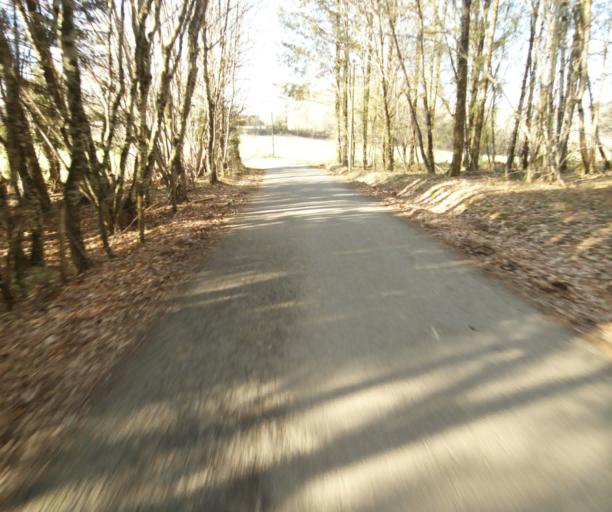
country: FR
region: Limousin
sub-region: Departement de la Correze
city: Saint-Clement
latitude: 45.3748
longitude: 1.6248
